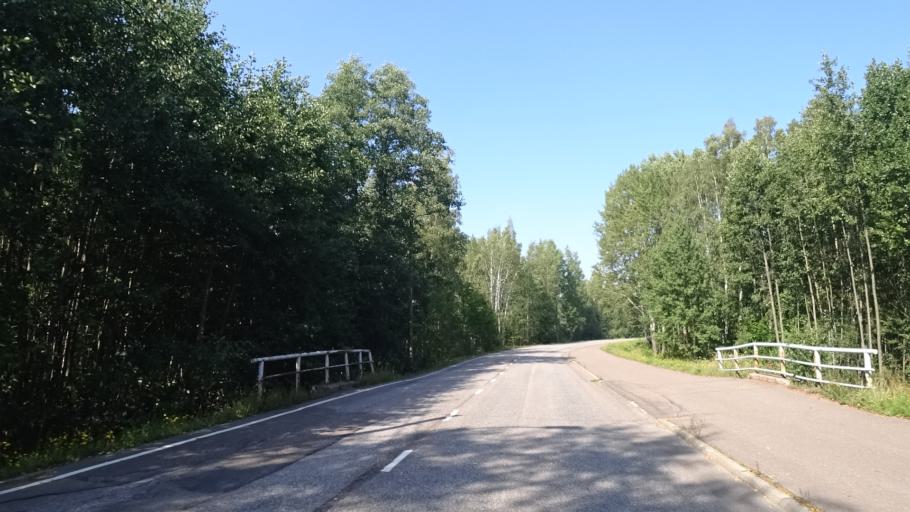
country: FI
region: Kymenlaakso
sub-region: Kotka-Hamina
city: Karhula
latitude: 60.5044
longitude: 26.9482
